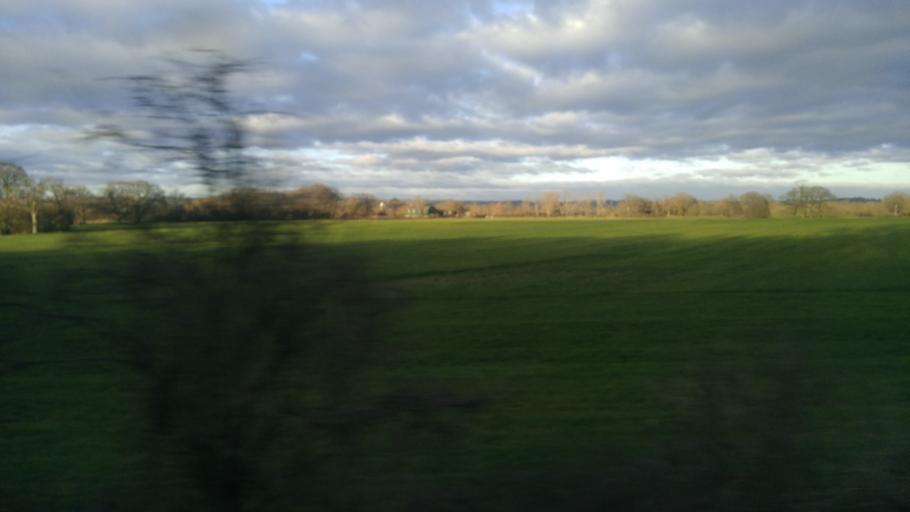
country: GB
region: England
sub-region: Kent
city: Headcorn
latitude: 51.1620
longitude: 0.6754
